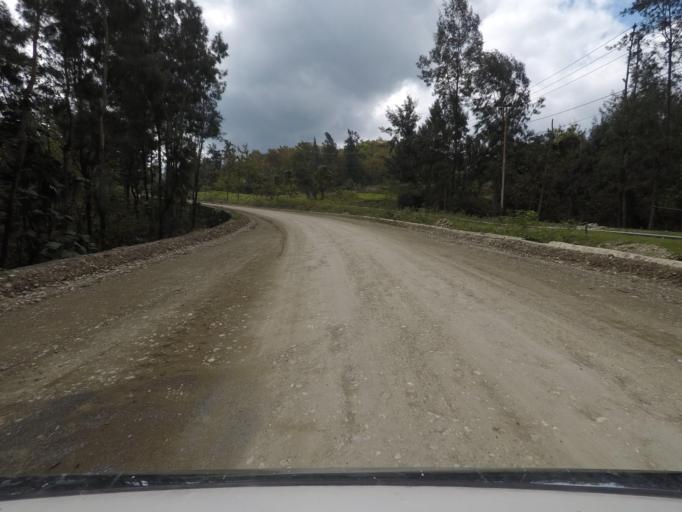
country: TL
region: Viqueque
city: Viqueque
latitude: -8.7955
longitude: 126.3781
